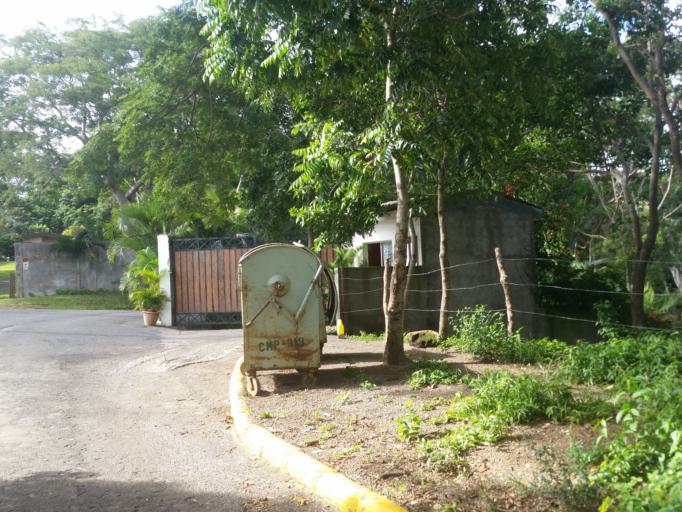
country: NI
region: Masaya
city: Ticuantepe
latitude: 12.0582
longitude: -86.2601
